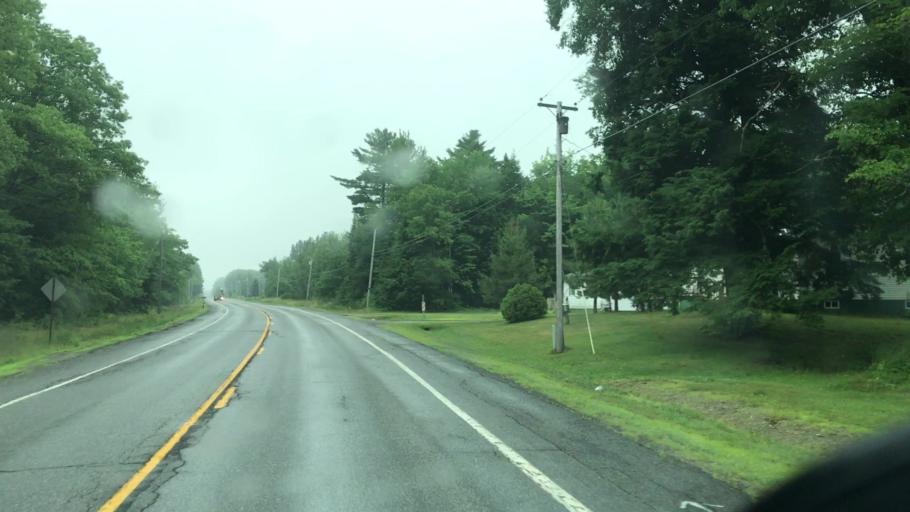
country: US
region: Maine
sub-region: Penobscot County
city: Howland
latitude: 45.2693
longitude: -68.6388
